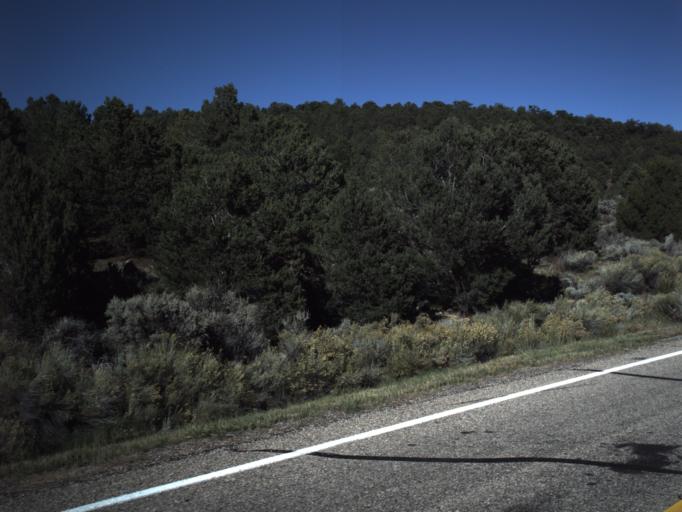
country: US
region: Utah
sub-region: Garfield County
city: Panguitch
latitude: 37.7616
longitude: -112.5111
